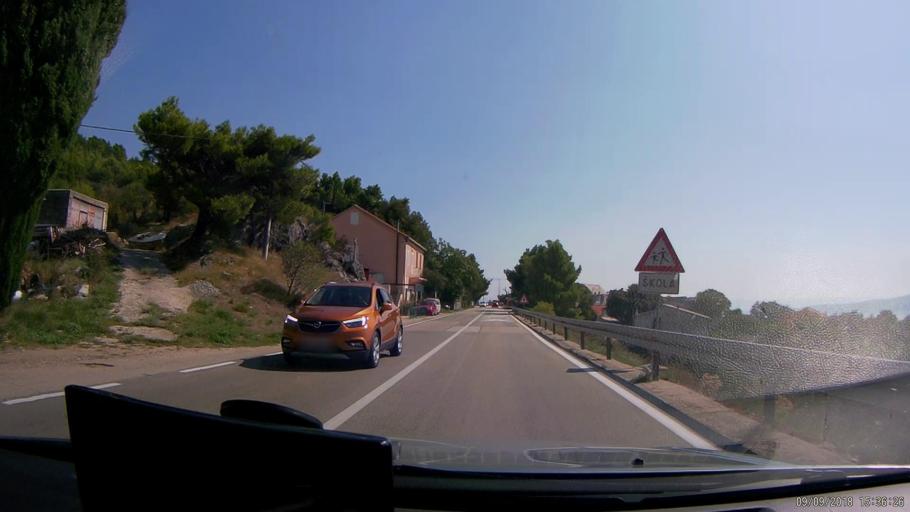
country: HR
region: Splitsko-Dalmatinska
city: Donja Brela
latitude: 43.3782
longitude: 16.9228
